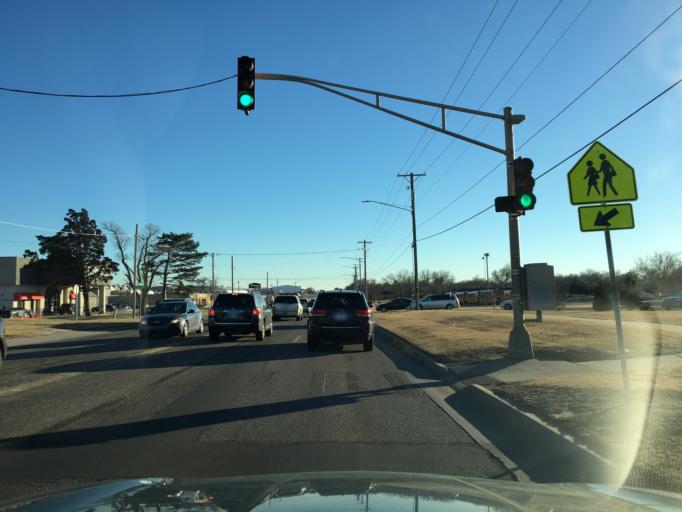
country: US
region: Kansas
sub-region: Sedgwick County
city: Bellaire
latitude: 37.6972
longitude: -97.2263
